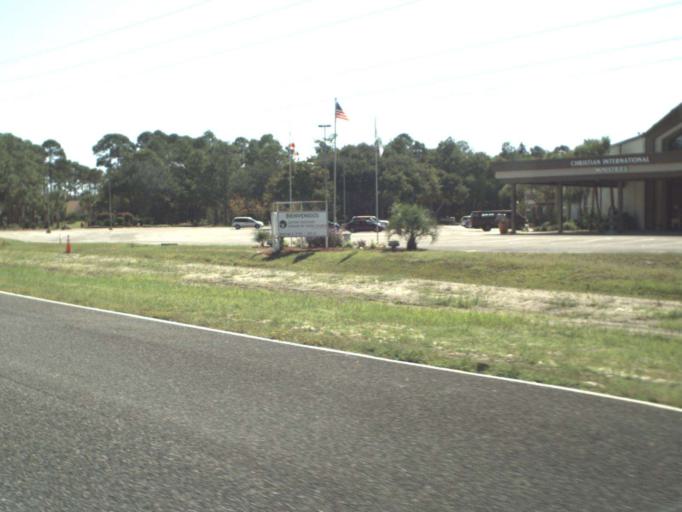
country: US
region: Florida
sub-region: Walton County
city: Seaside
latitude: 30.3560
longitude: -86.0981
